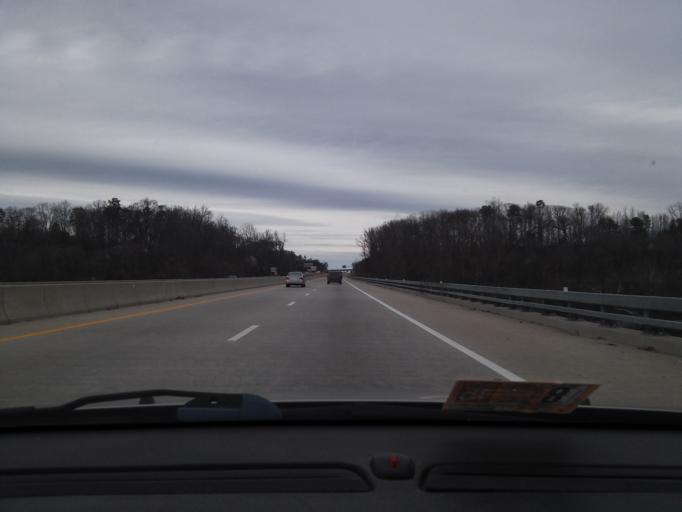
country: US
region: Virginia
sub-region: Henrico County
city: Short Pump
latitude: 37.5759
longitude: -77.6797
